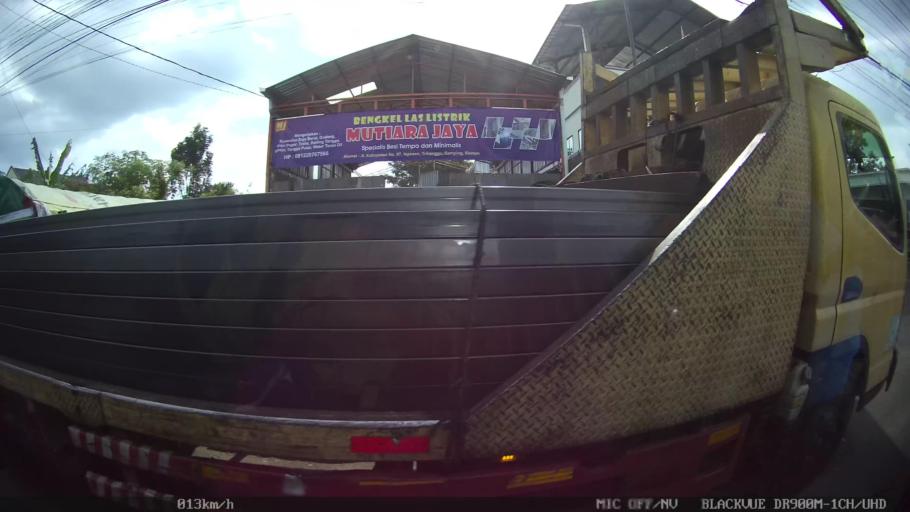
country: ID
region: Daerah Istimewa Yogyakarta
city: Melati
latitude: -7.7465
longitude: 110.3486
